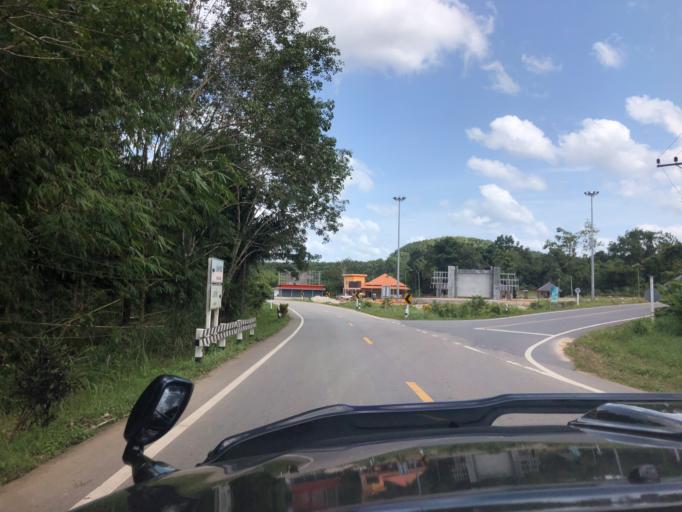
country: TH
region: Krabi
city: Khlong Thom
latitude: 7.9497
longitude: 99.2057
